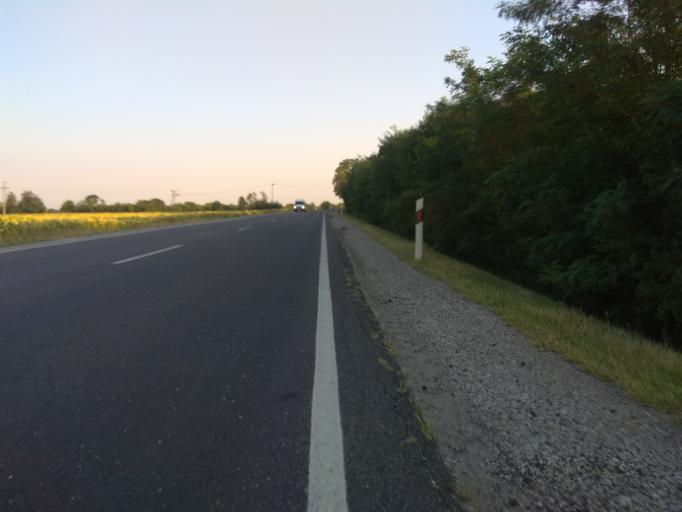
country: HU
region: Borsod-Abauj-Zemplen
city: Nyekladhaza
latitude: 47.9677
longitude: 20.8321
